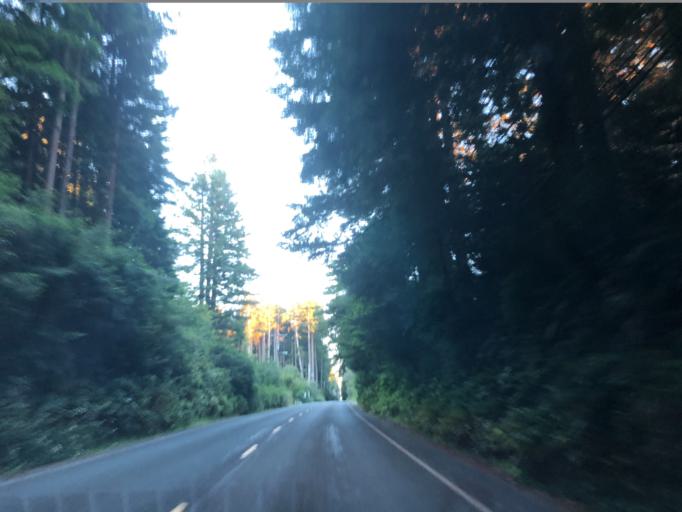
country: US
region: California
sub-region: Humboldt County
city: Westhaven-Moonstone
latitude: 41.0879
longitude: -124.1500
